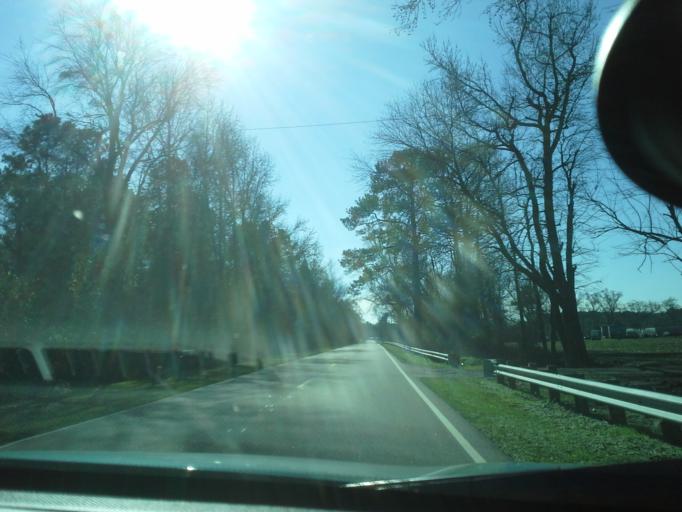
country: US
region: North Carolina
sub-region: Beaufort County
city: Belhaven
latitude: 35.6001
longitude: -76.6627
